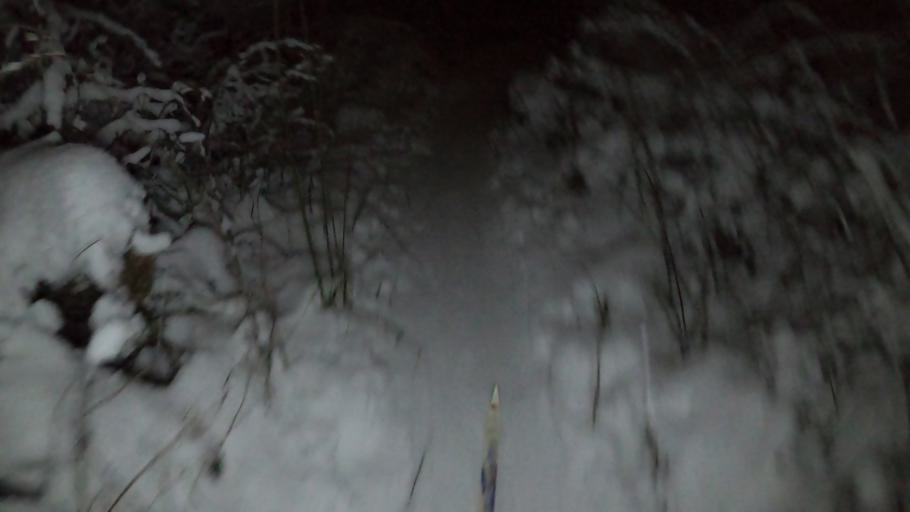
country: RU
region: Moskovskaya
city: Opalikha
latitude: 55.8625
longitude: 37.2334
